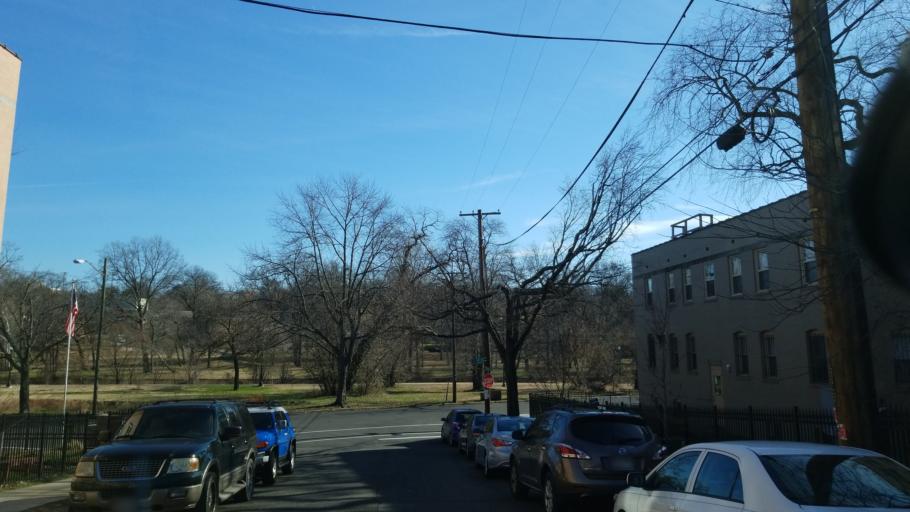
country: US
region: Maryland
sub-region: Prince George's County
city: Glassmanor
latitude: 38.8342
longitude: -77.0033
